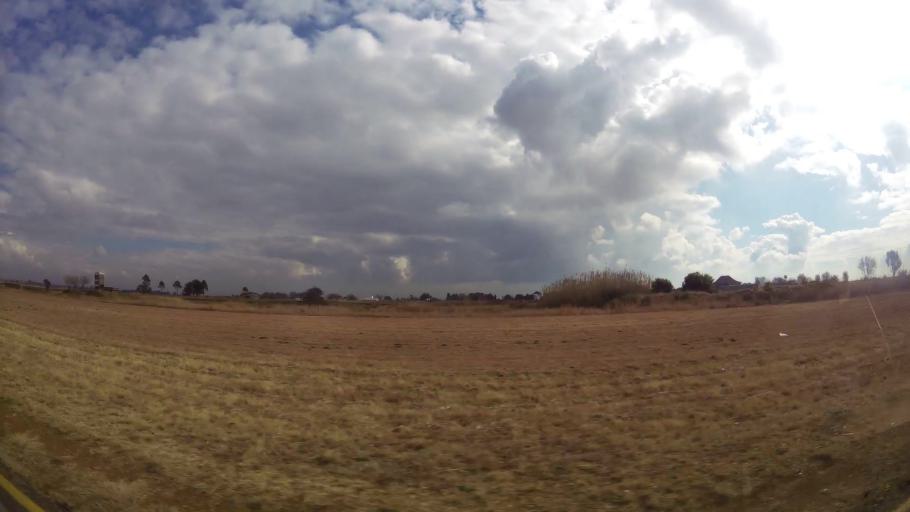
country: ZA
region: Gauteng
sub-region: Sedibeng District Municipality
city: Meyerton
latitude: -26.6174
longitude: 28.0597
